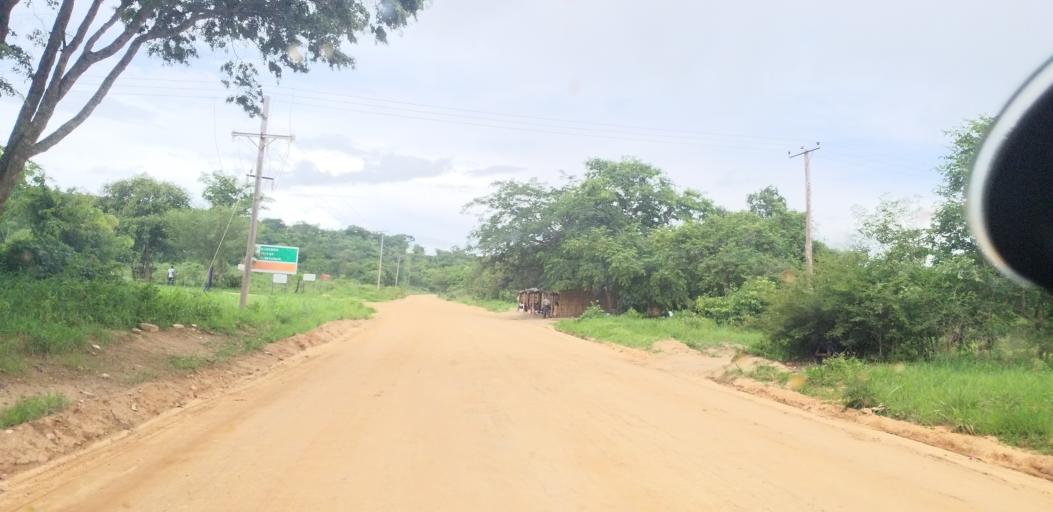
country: ZM
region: Lusaka
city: Chongwe
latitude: -15.1839
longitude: 28.4485
